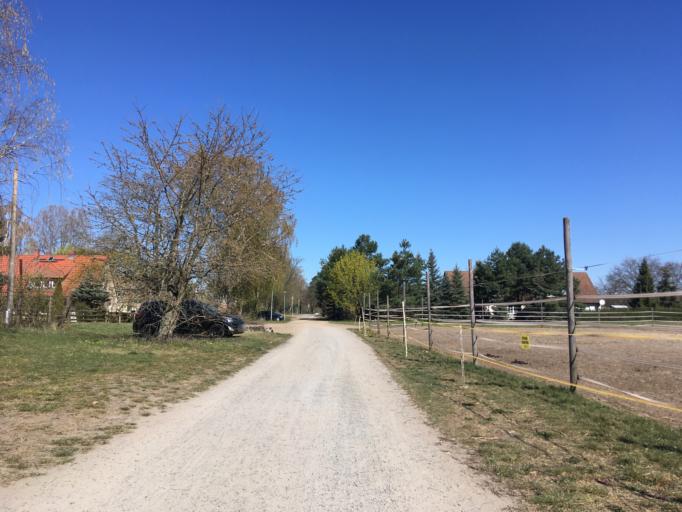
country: DE
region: Berlin
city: Buch
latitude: 52.6770
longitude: 13.4786
